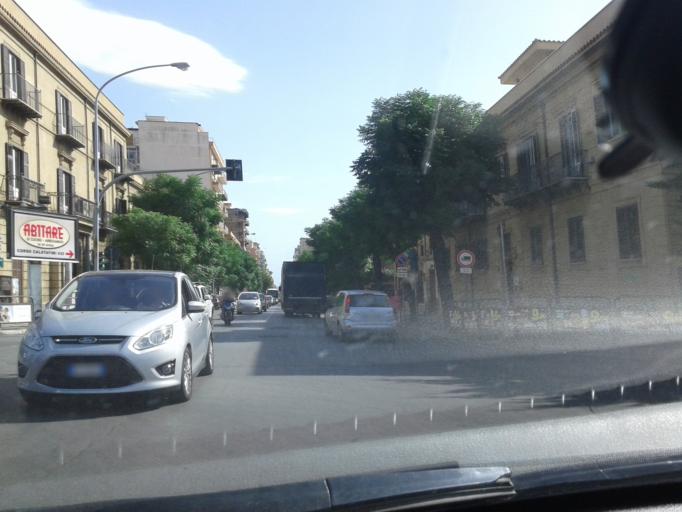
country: IT
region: Sicily
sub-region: Palermo
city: Palermo
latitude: 38.1033
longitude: 13.3308
